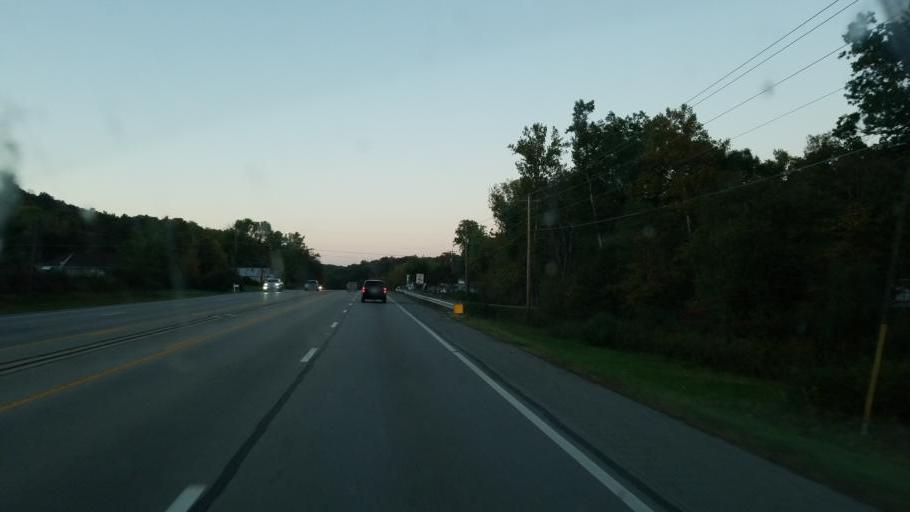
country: US
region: Ohio
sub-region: Ross County
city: Chillicothe
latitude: 39.2365
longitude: -82.9842
